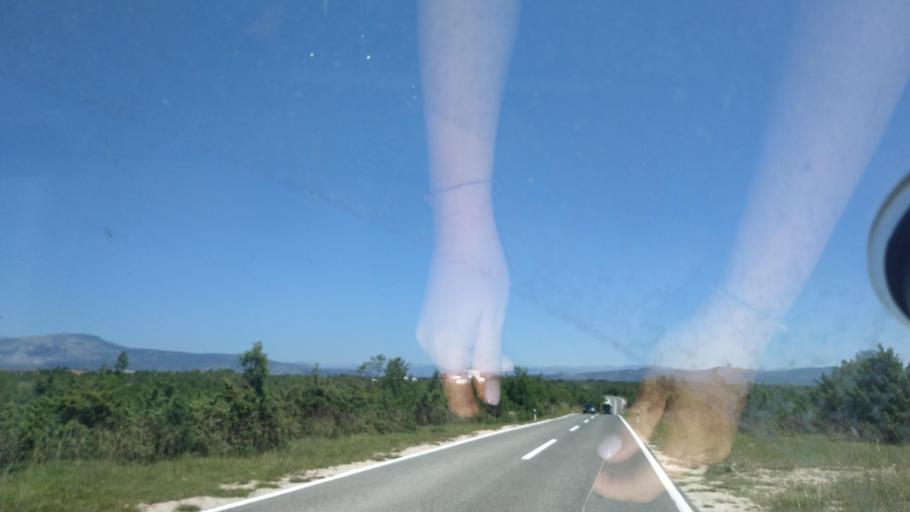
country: HR
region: Sibensko-Kniniska
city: Drnis
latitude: 43.8195
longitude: 16.0648
